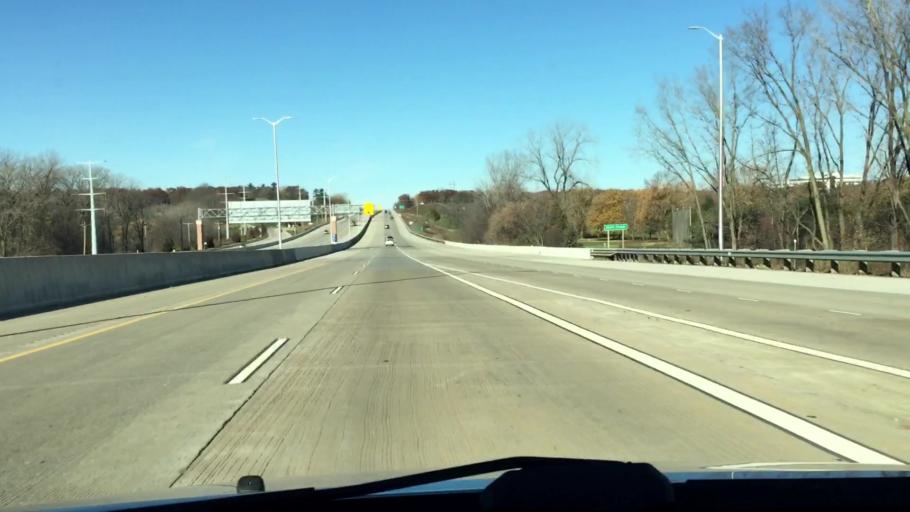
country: US
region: Wisconsin
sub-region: Brown County
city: Howard
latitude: 44.5454
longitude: -88.0936
